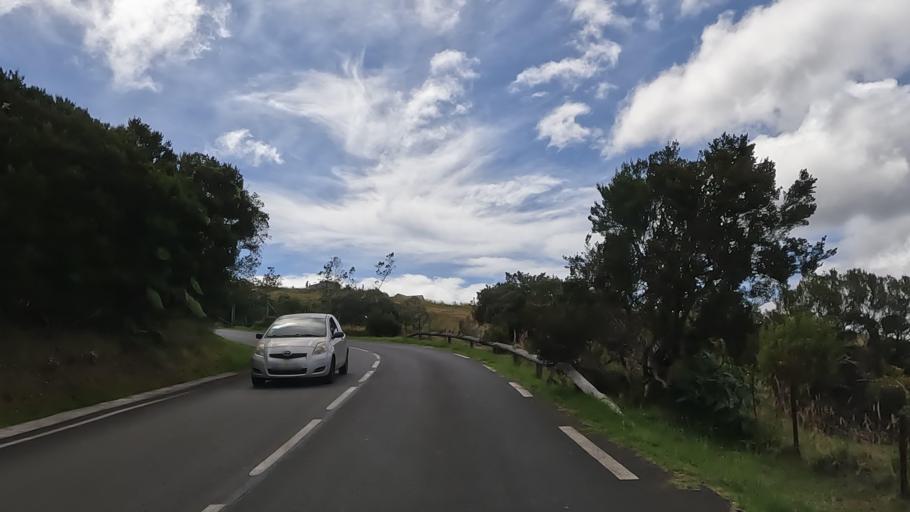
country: RE
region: Reunion
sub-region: Reunion
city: Le Tampon
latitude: -21.2446
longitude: 55.5896
